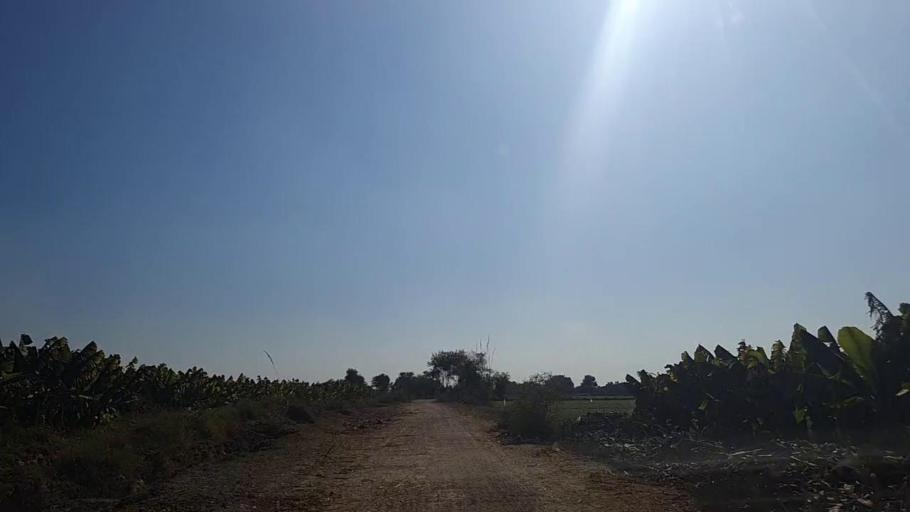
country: PK
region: Sindh
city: Sakrand
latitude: 26.2380
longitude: 68.1998
